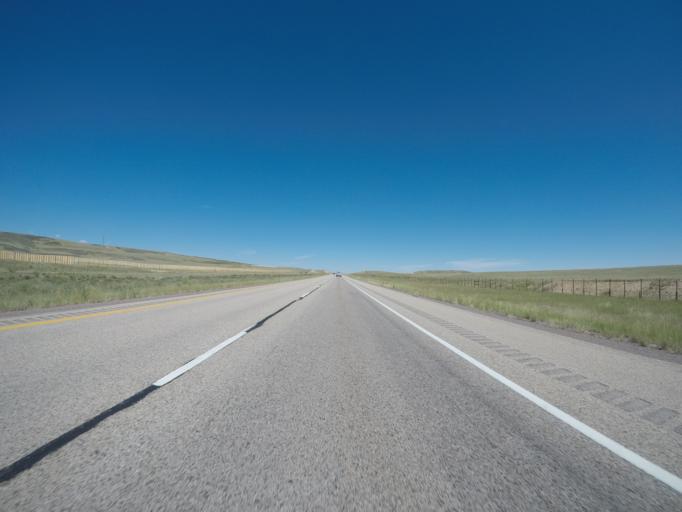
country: US
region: Wyoming
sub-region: Albany County
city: Laramie
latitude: 41.4890
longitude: -106.0328
